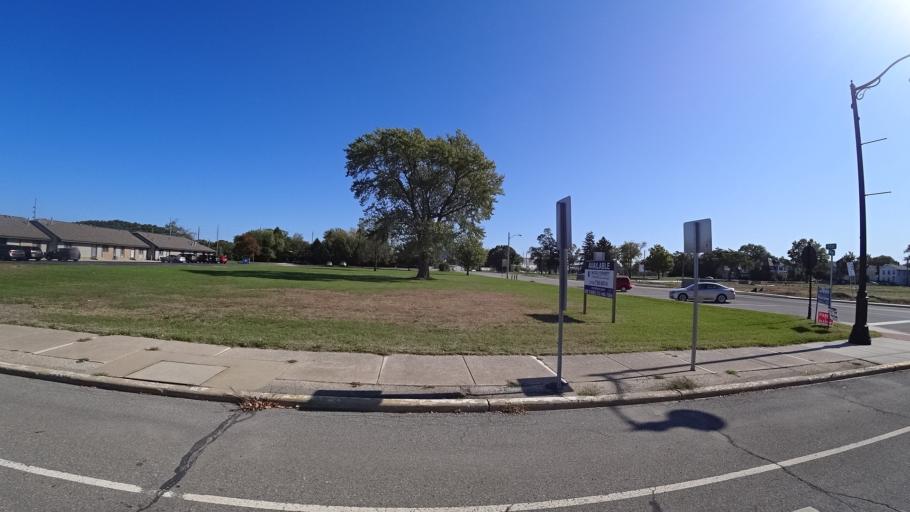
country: US
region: Indiana
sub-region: LaPorte County
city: Michigan City
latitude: 41.7179
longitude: -86.9005
